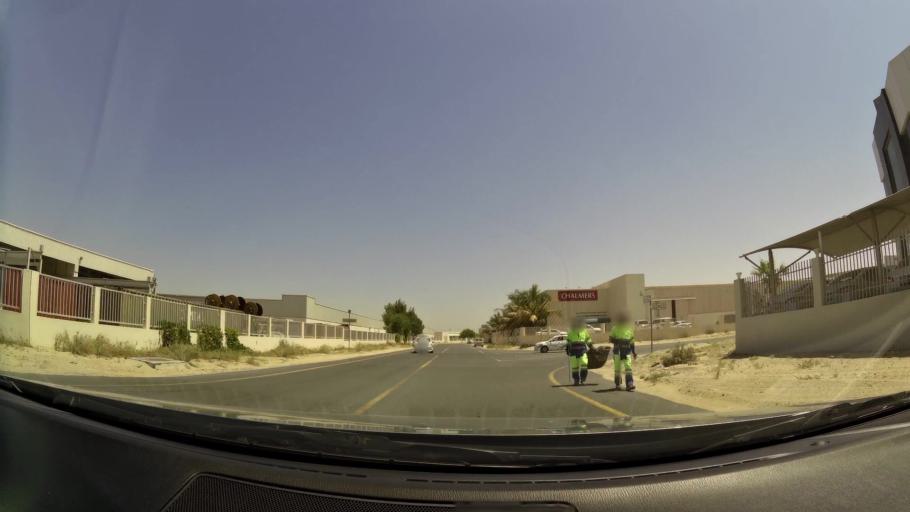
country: AE
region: Dubai
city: Dubai
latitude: 24.9775
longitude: 55.1901
